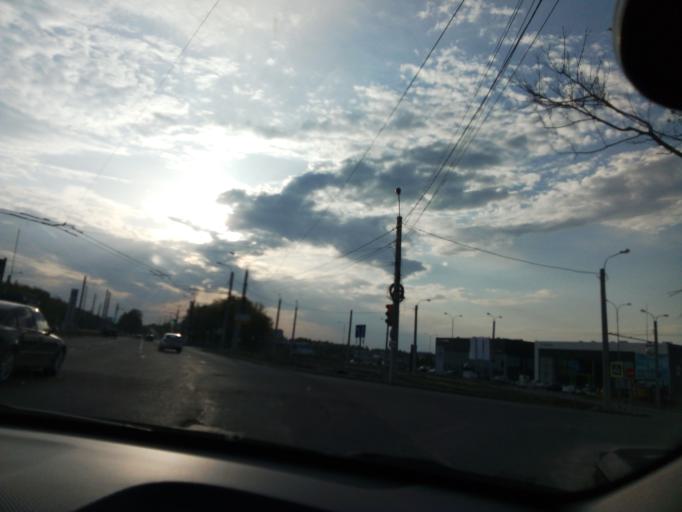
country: RU
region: Chuvashia
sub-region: Cheboksarskiy Rayon
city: Cheboksary
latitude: 56.1259
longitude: 47.3639
